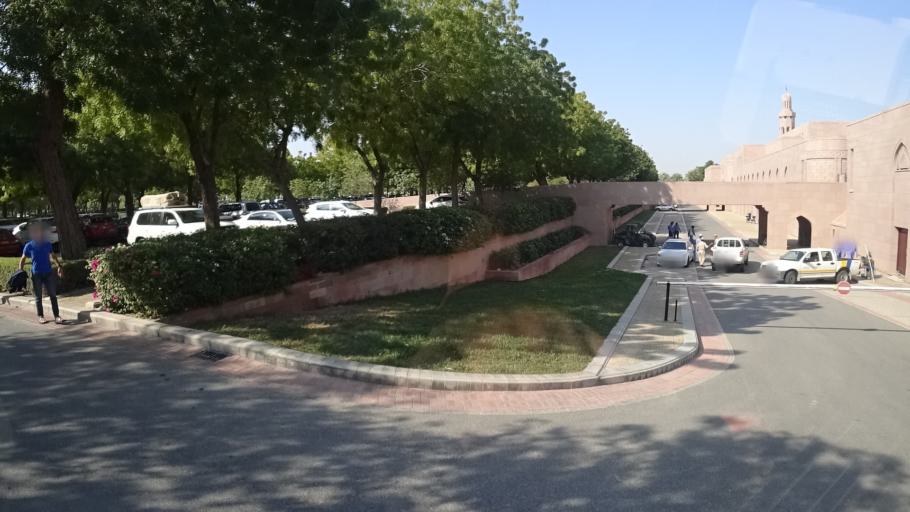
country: OM
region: Muhafazat Masqat
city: Bawshar
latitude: 23.5827
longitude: 58.3900
